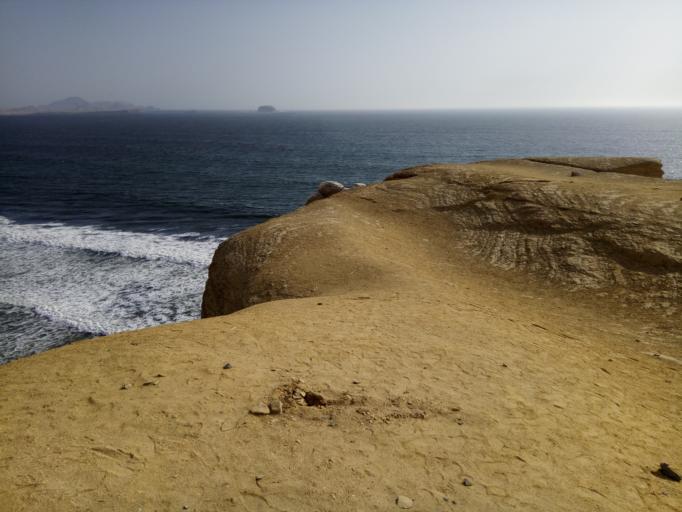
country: PE
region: Ica
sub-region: Provincia de Pisco
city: Paracas
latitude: -13.9375
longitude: -76.2840
